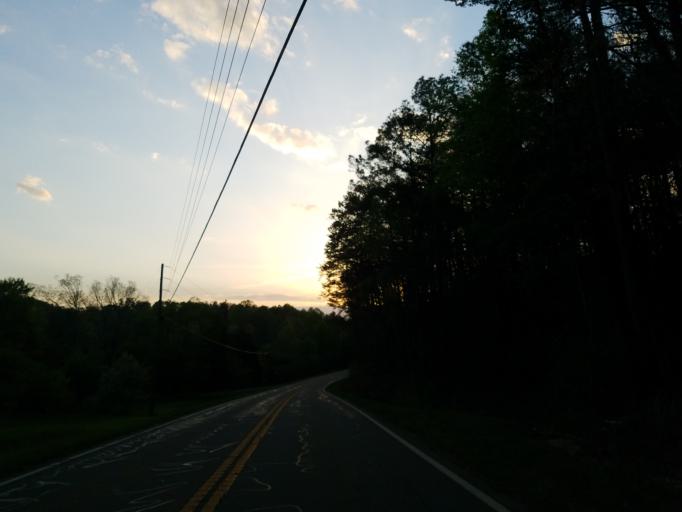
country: US
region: Georgia
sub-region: Pickens County
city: Jasper
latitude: 34.5129
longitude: -84.4518
